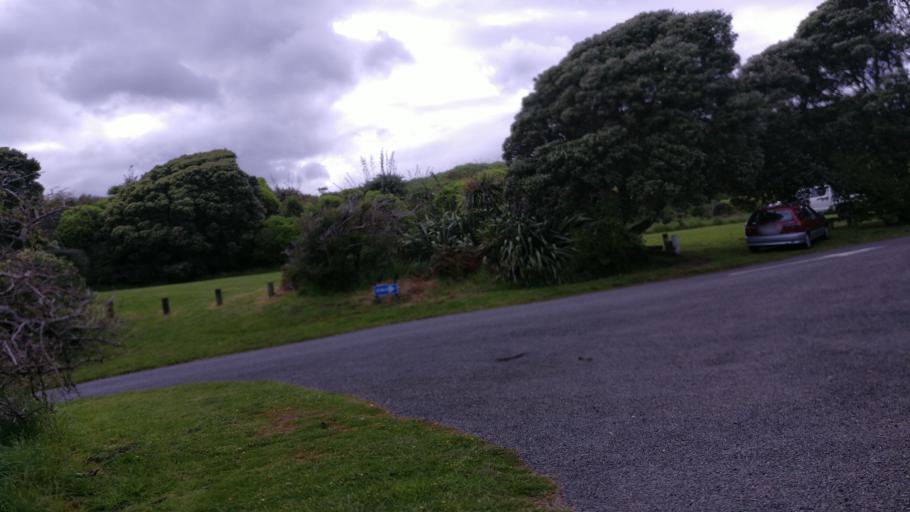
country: NZ
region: Wellington
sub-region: Kapiti Coast District
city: Paraparaumu
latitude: -40.9716
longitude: 174.9623
